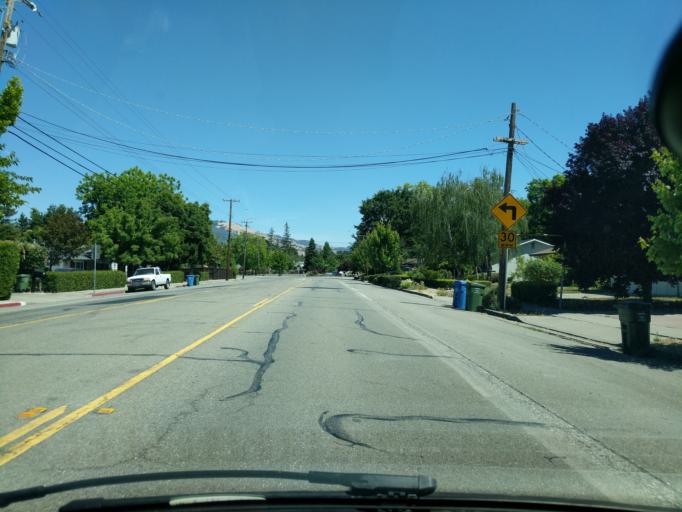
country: US
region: California
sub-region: Contra Costa County
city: Waldon
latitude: 37.9165
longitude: -122.0271
